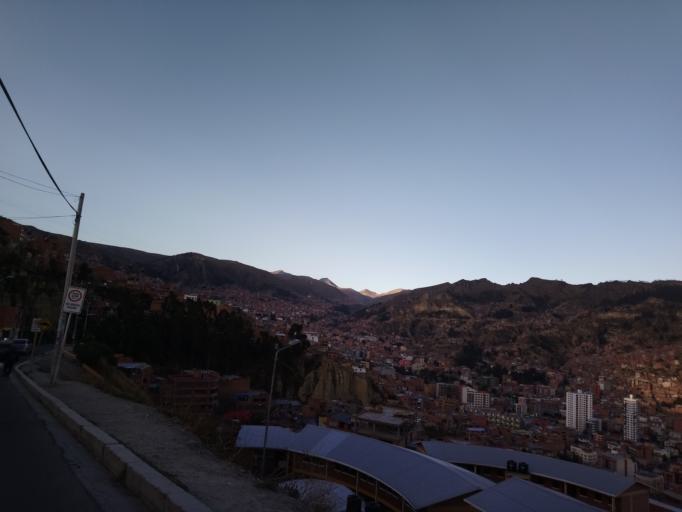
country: BO
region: La Paz
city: La Paz
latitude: -16.4887
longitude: -68.1282
